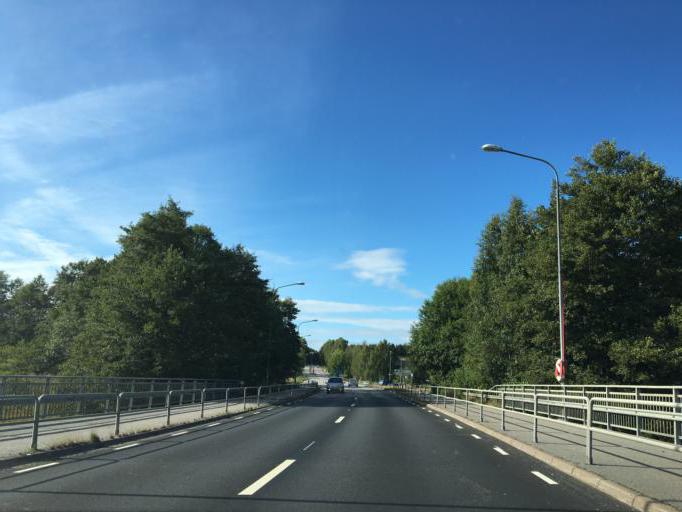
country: SE
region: Soedermanland
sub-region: Nykopings Kommun
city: Nykoping
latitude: 58.7754
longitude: 16.9802
